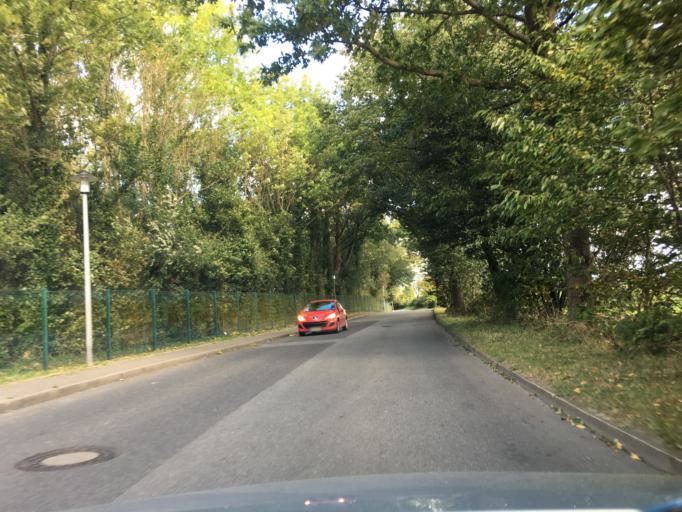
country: DE
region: Schleswig-Holstein
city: Laboe
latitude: 54.4104
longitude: 10.2331
